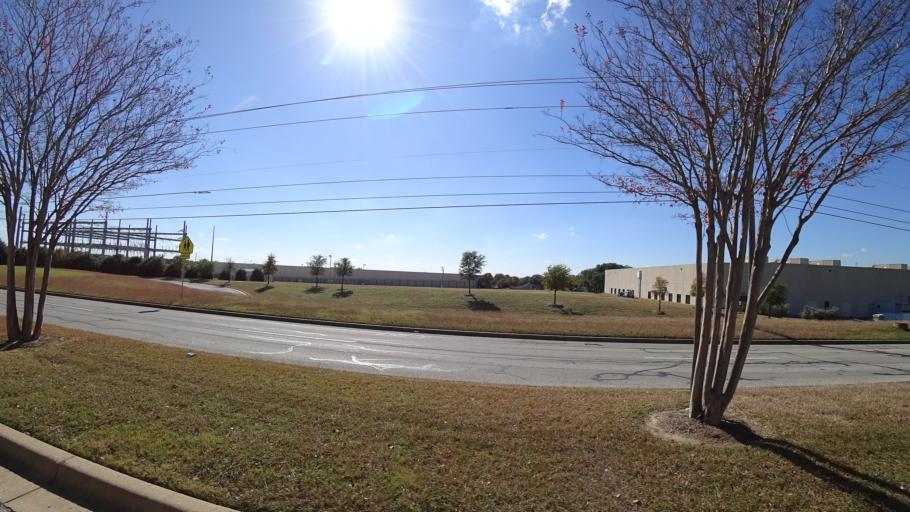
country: US
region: Texas
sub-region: Travis County
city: Wells Branch
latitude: 30.4473
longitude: -97.6897
